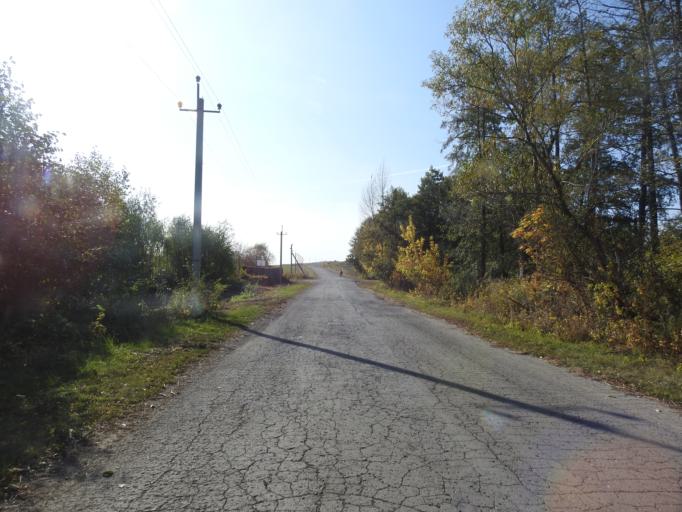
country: RU
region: Saratov
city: Baltay
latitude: 52.4702
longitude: 46.6706
